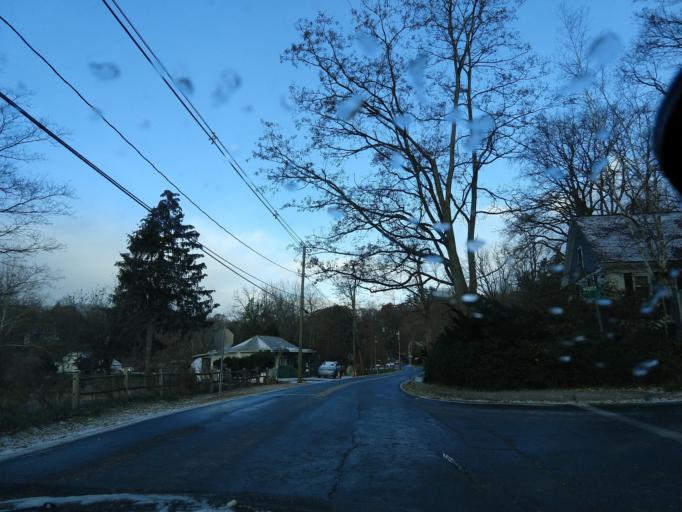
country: US
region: New York
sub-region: Tompkins County
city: East Ithaca
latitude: 42.4520
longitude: -76.4683
